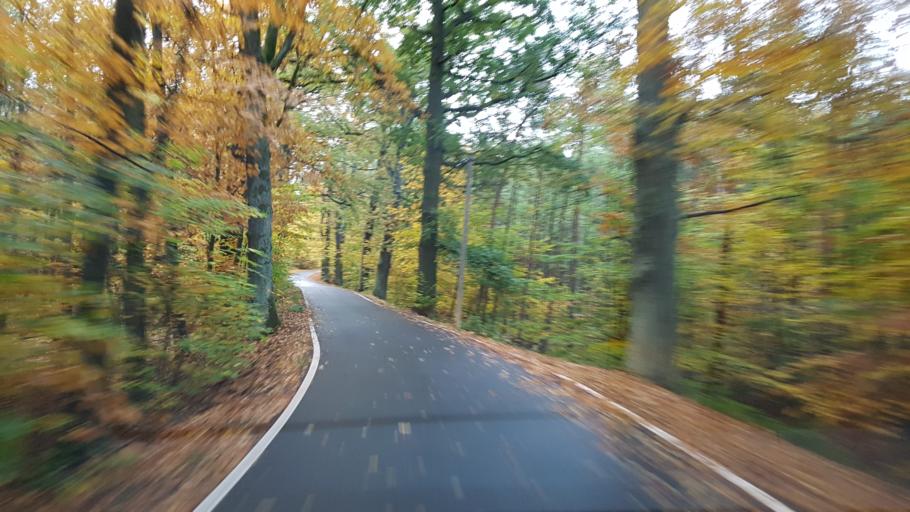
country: DE
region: Saxony
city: Cavertitz
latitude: 51.3957
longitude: 13.0643
